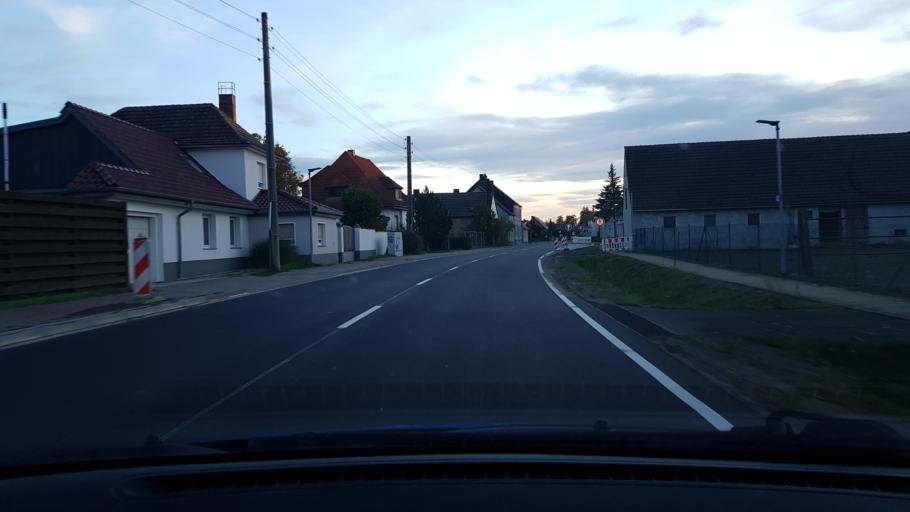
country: DE
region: Saxony-Anhalt
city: Wahlitz
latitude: 52.1065
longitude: 11.7812
